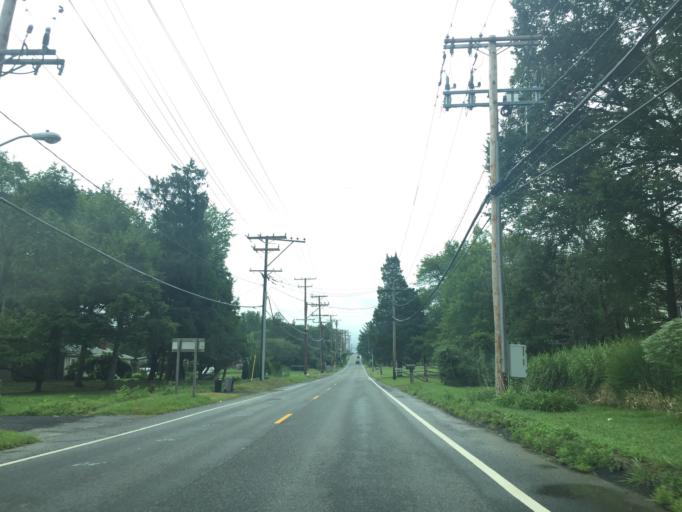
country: US
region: Maryland
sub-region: Harford County
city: Edgewood
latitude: 39.4454
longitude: -76.3081
